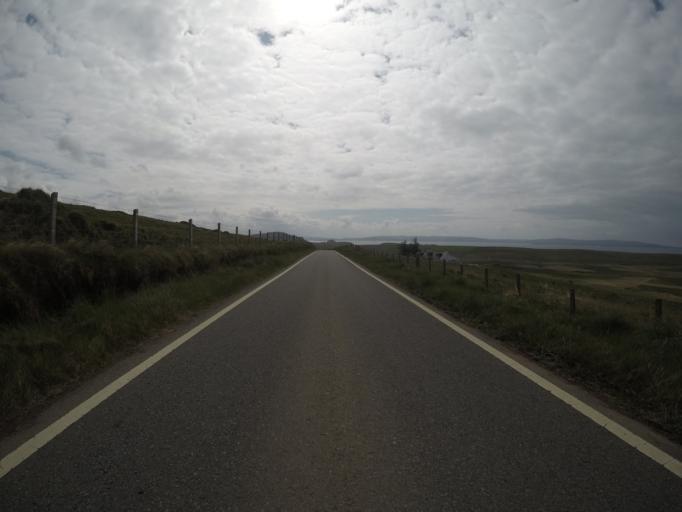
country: GB
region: Scotland
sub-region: Highland
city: Portree
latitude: 57.6319
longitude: -6.3778
